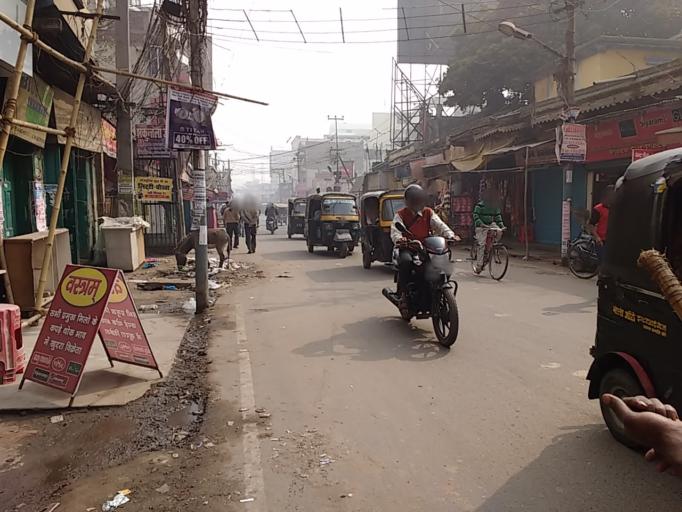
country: IN
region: Bihar
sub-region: Patna
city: Patna
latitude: 25.6152
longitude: 85.1513
